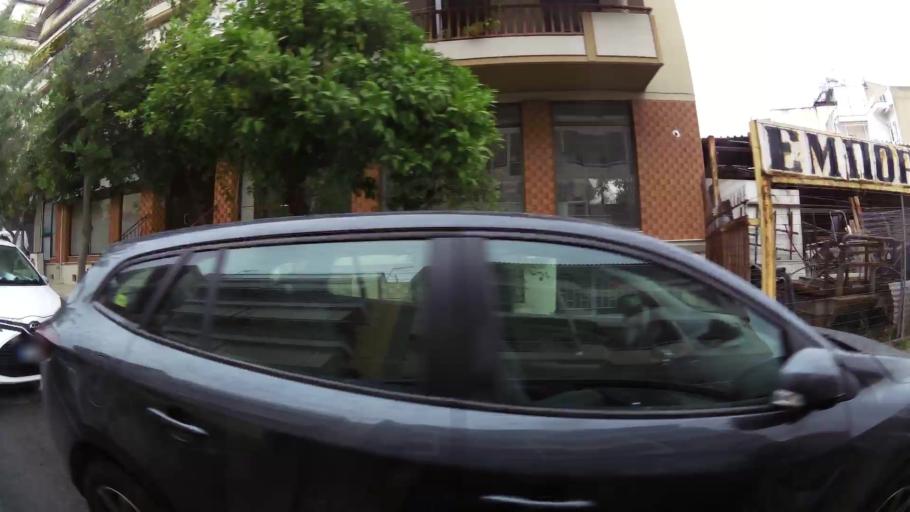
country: GR
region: Attica
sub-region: Nomos Piraios
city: Korydallos
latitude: 37.9850
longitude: 23.6445
